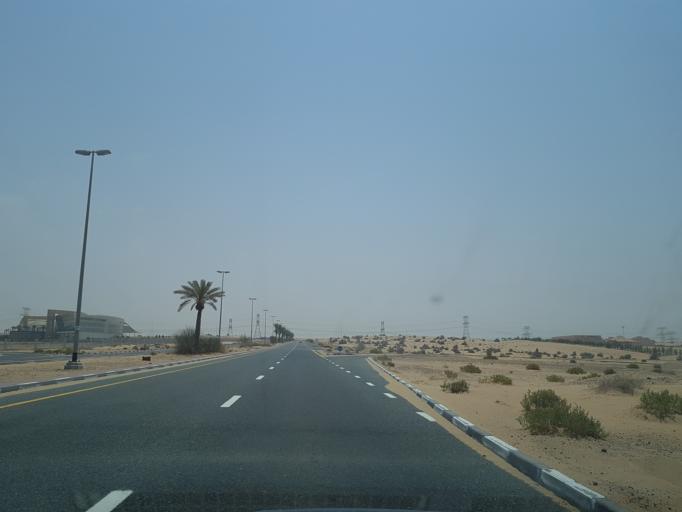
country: AE
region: Ash Shariqah
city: Sharjah
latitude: 25.1091
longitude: 55.4096
